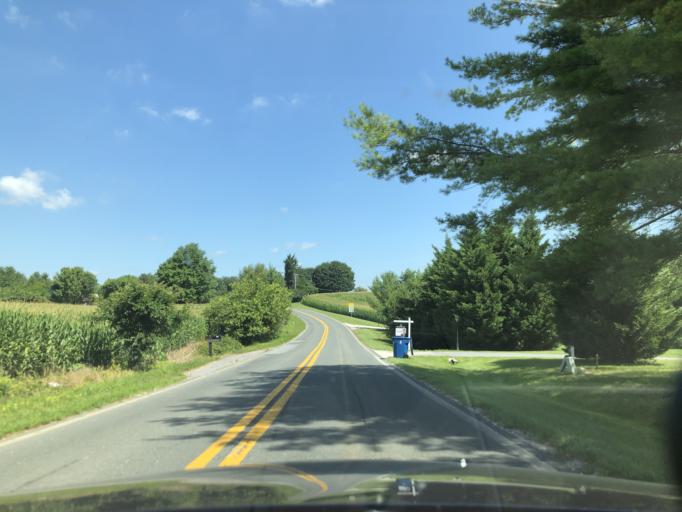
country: US
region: Maryland
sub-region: Carroll County
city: Westminster
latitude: 39.6013
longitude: -76.9677
